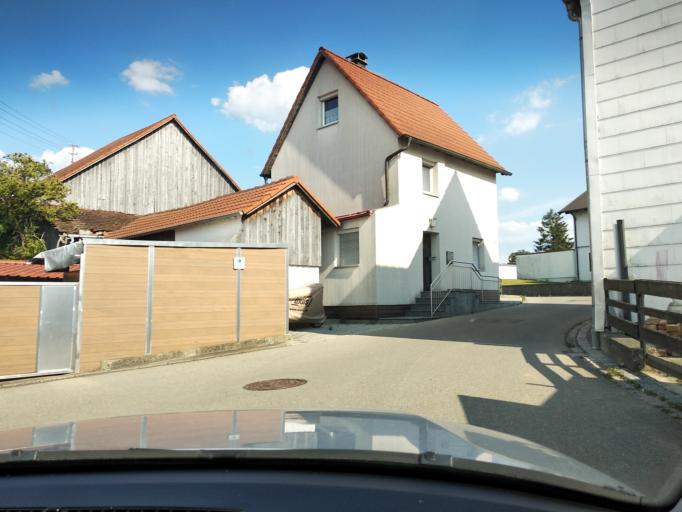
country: DE
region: Bavaria
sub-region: Swabia
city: Trunkelsberg
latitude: 48.0022
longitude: 10.2156
